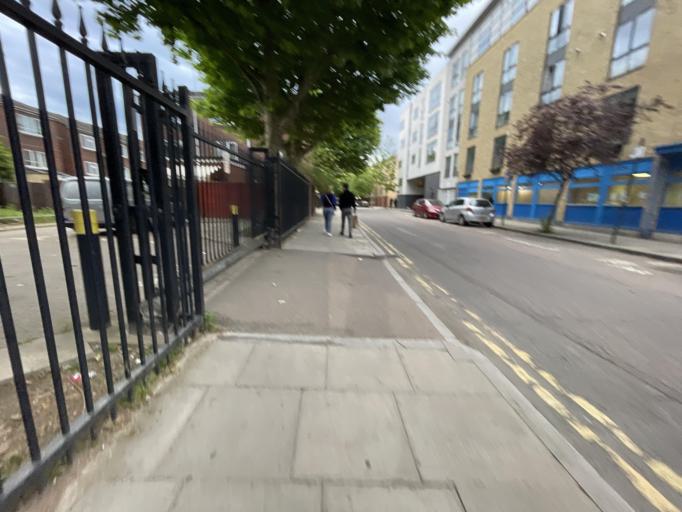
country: GB
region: England
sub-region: Greater London
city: Bethnal Green
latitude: 51.5175
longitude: -0.0697
